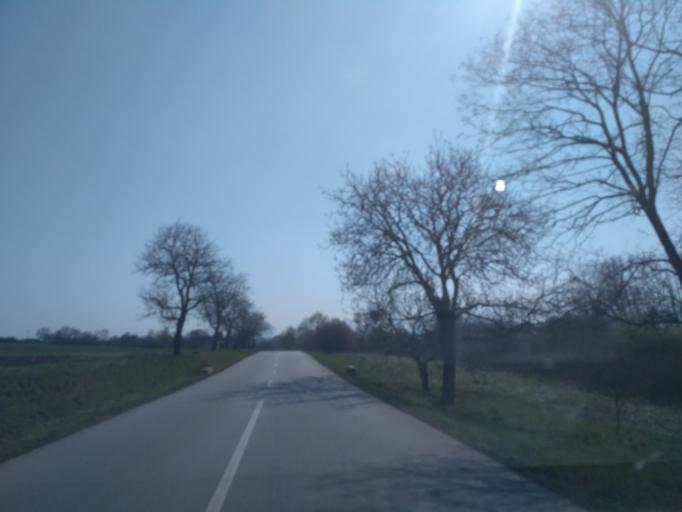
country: SK
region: Kosicky
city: Secovce
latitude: 48.6705
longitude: 21.6124
